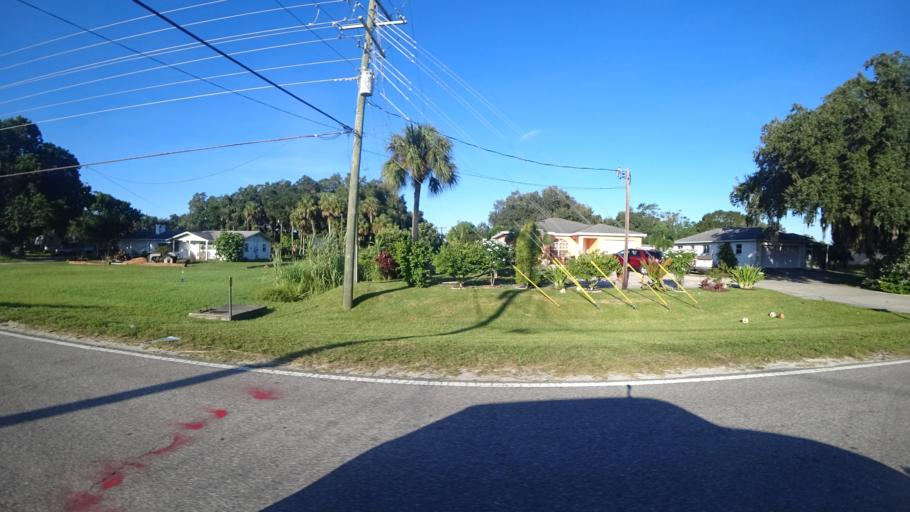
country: US
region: Florida
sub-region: Manatee County
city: Ellenton
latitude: 27.5645
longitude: -82.5279
